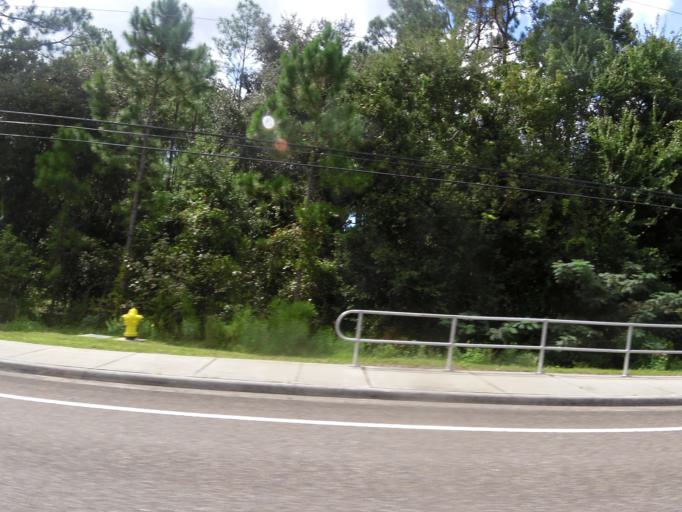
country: US
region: Florida
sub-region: Clay County
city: Green Cove Springs
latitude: 29.9559
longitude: -81.4951
